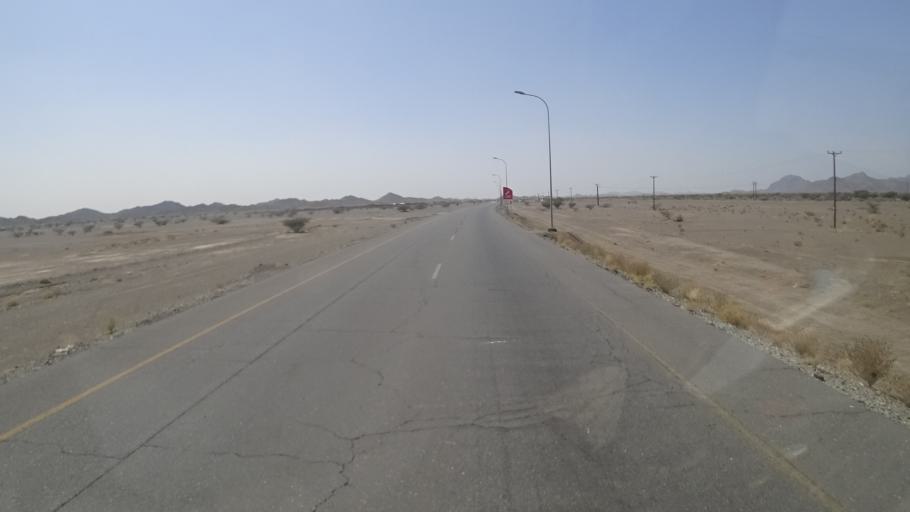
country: OM
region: Ash Sharqiyah
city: Ibra'
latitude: 22.6457
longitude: 58.5097
